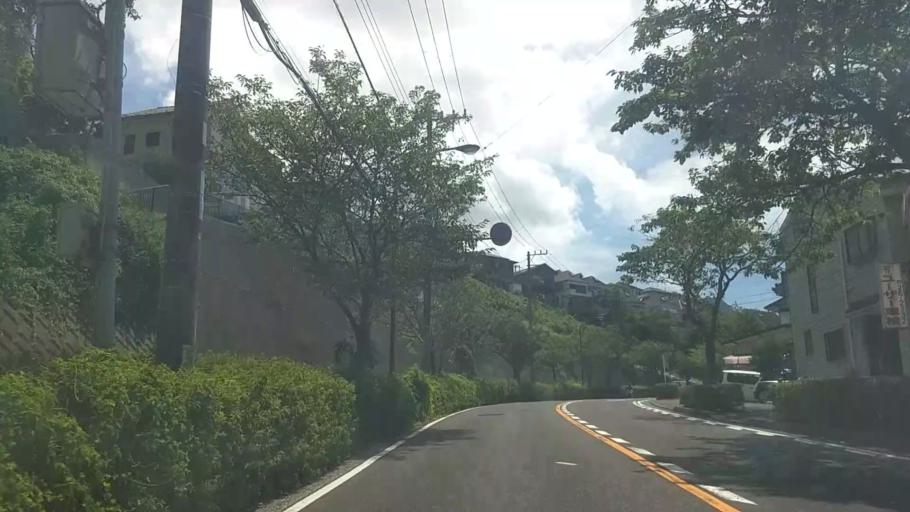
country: JP
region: Kanagawa
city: Yokosuka
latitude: 35.2734
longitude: 139.6489
